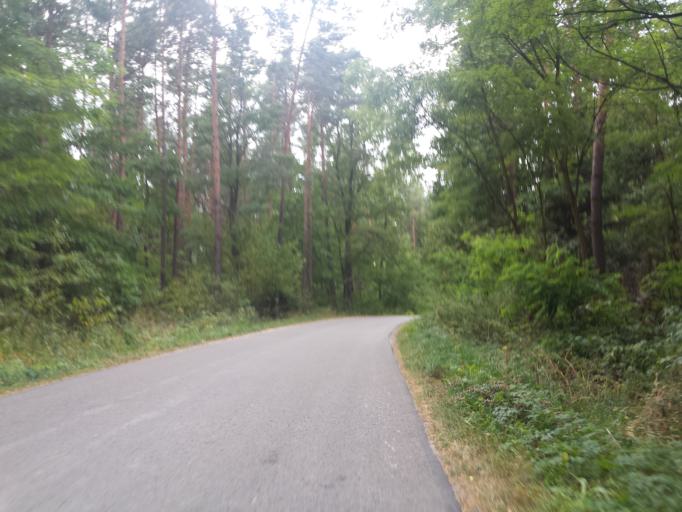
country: PL
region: Swietokrzyskie
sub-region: Powiat staszowski
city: Bogoria
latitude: 50.6557
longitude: 21.2190
